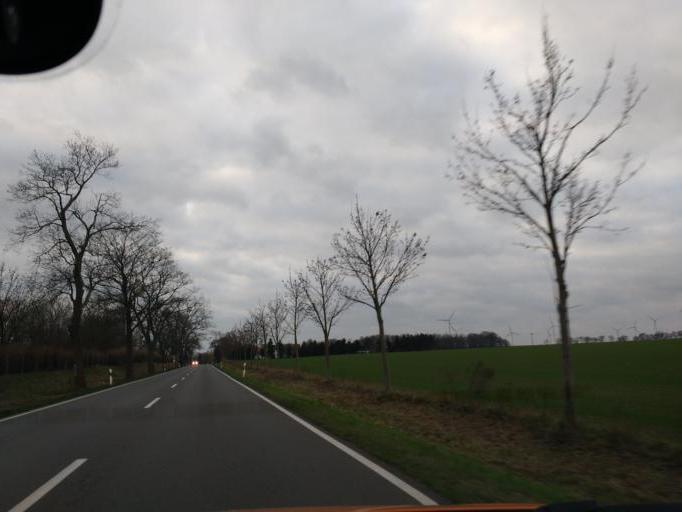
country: DE
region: Brandenburg
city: Wriezen
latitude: 52.6933
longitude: 14.1058
